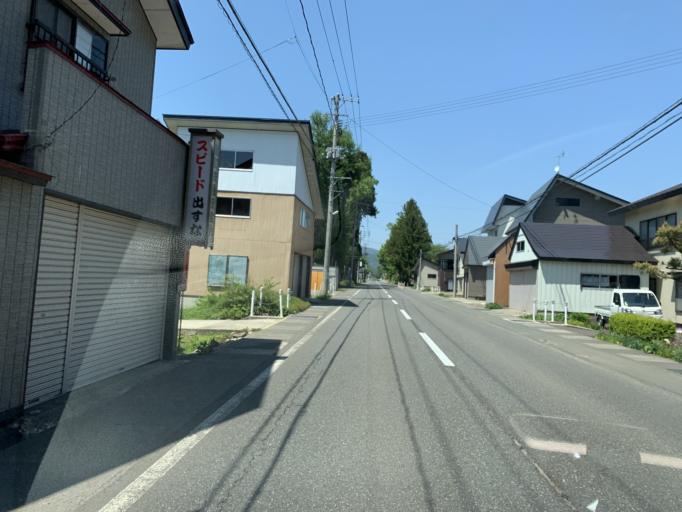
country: JP
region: Akita
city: Yokotemachi
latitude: 39.3940
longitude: 140.7580
